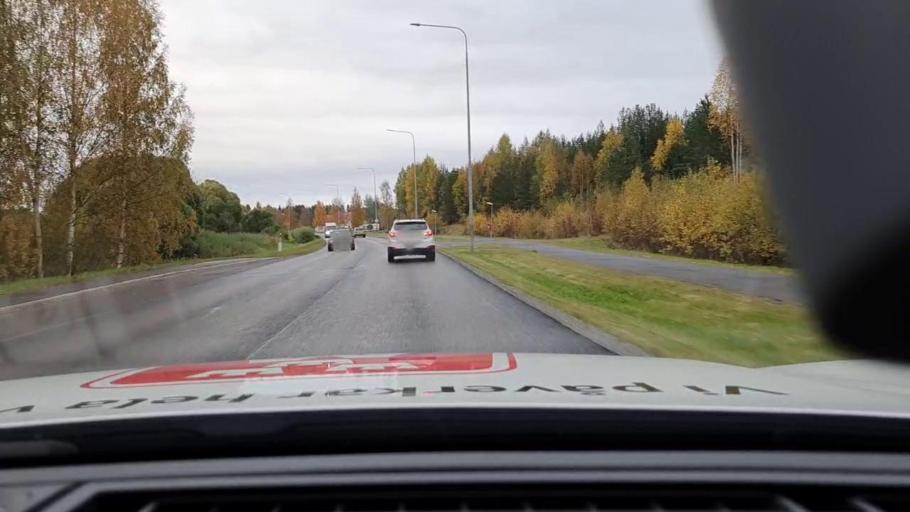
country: SE
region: Norrbotten
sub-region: Bodens Kommun
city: Saevast
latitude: 65.7597
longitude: 21.7403
